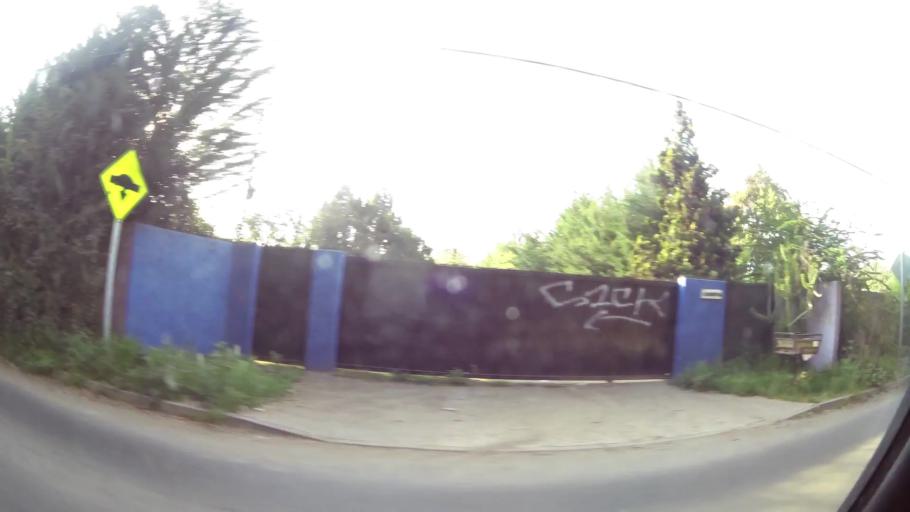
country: CL
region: Santiago Metropolitan
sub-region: Provincia de Maipo
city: San Bernardo
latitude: -33.5600
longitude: -70.7723
